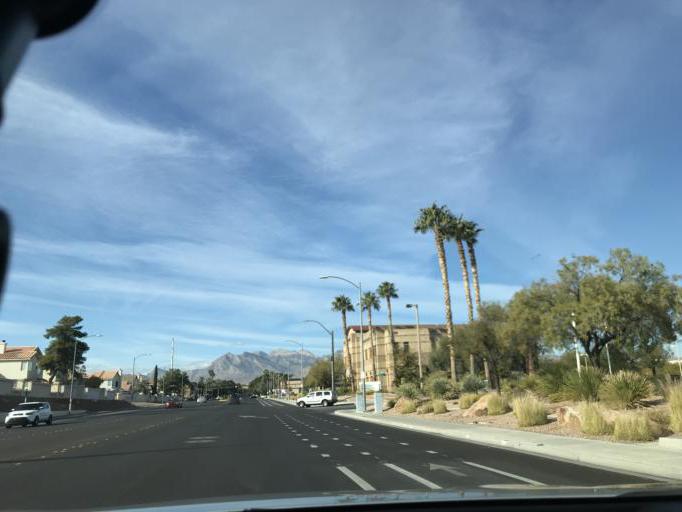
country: US
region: Nevada
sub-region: Clark County
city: Spring Valley
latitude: 36.2036
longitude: -115.2567
